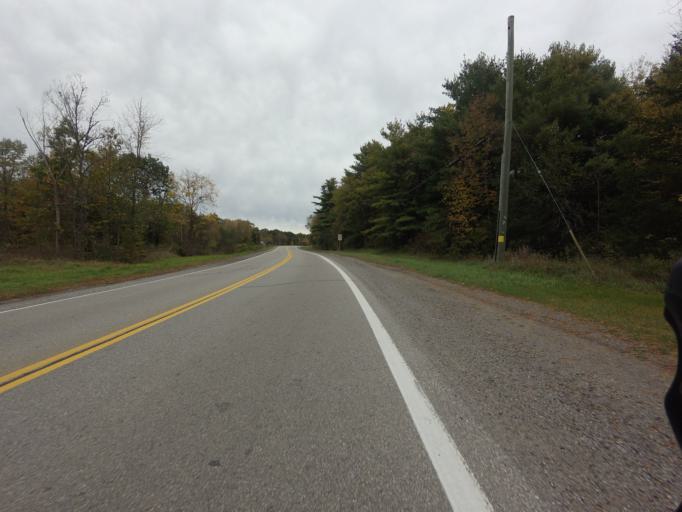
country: CA
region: Ontario
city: Gananoque
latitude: 44.5534
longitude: -76.1199
